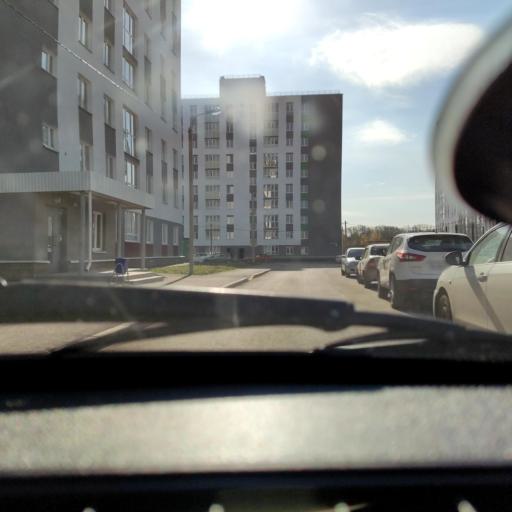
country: RU
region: Bashkortostan
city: Ufa
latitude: 54.6912
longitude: 55.9685
